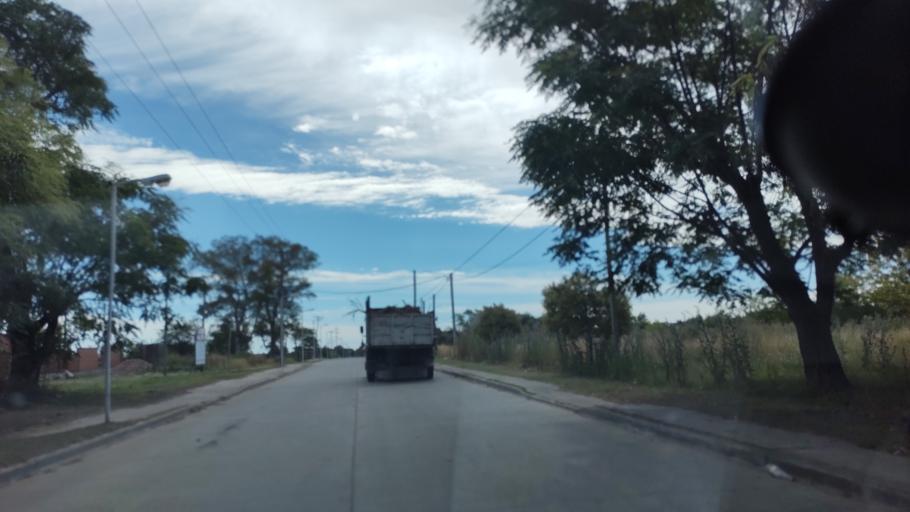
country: AR
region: Buenos Aires
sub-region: Partido de Lobos
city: Lobos
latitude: -35.1775
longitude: -59.1000
